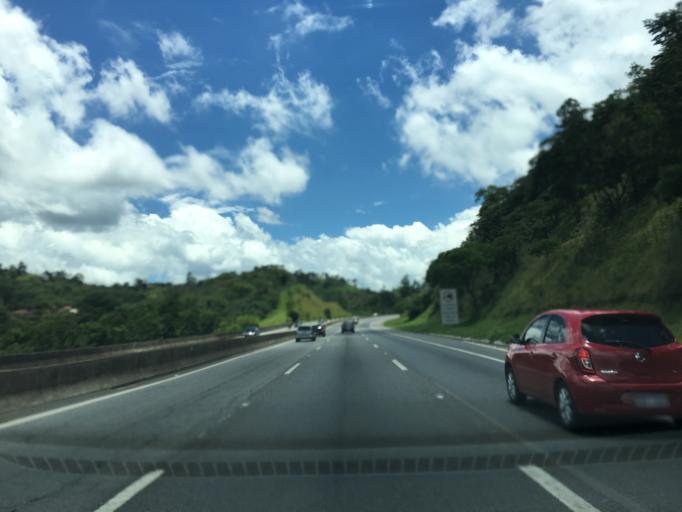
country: BR
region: Sao Paulo
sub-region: Mairipora
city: Mairipora
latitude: -23.2270
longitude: -46.5982
